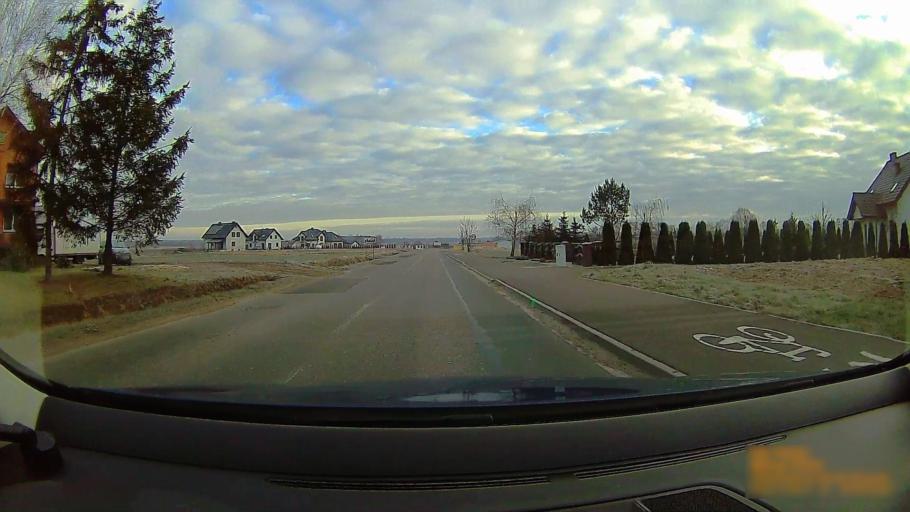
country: PL
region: Greater Poland Voivodeship
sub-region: Powiat koninski
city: Golina
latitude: 52.1900
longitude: 18.1175
